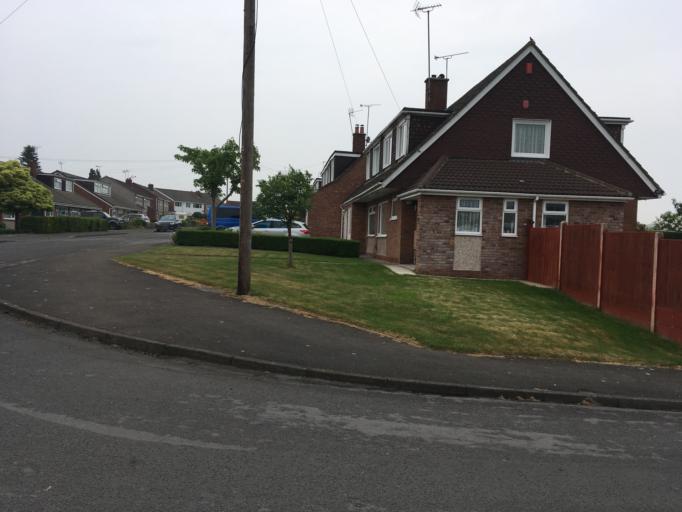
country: GB
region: England
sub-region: South Gloucestershire
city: Thornbury
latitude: 51.6103
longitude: -2.5186
